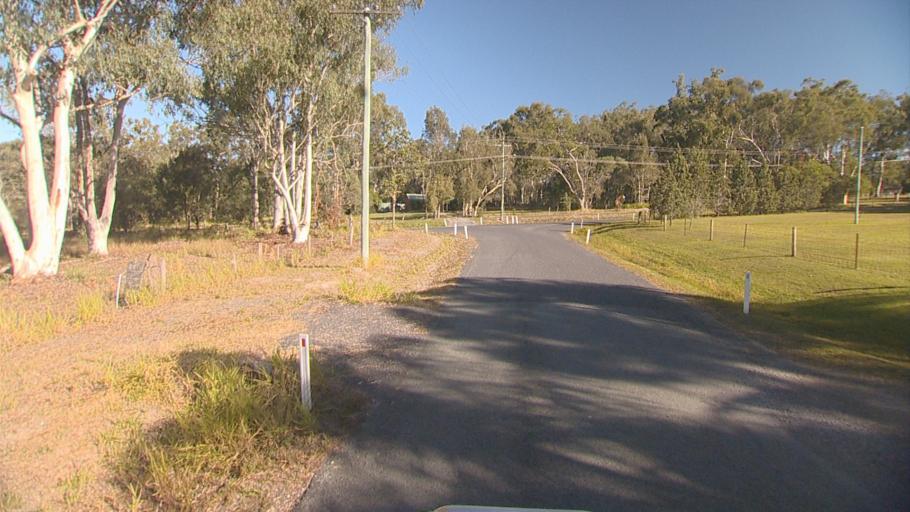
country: AU
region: Queensland
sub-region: Logan
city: Logan Reserve
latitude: -27.7327
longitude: 153.0820
